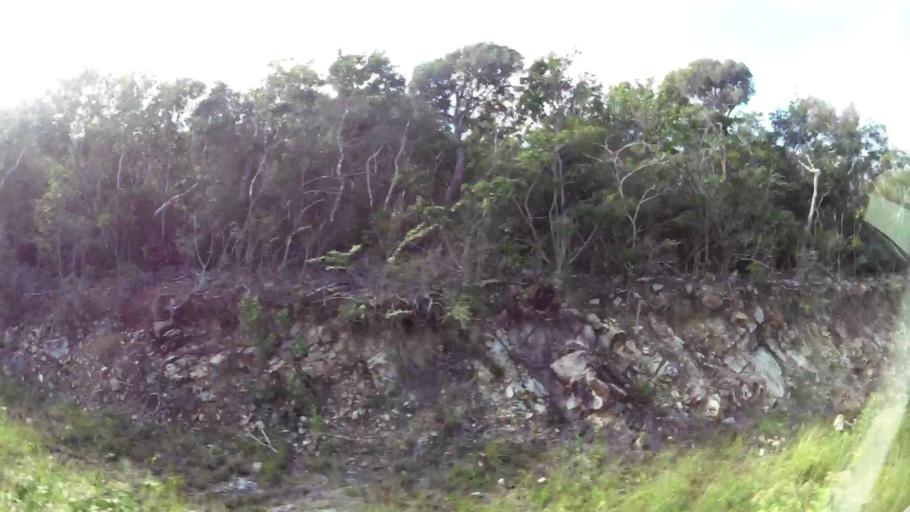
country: VG
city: Tortola
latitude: 18.4966
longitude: -64.4032
